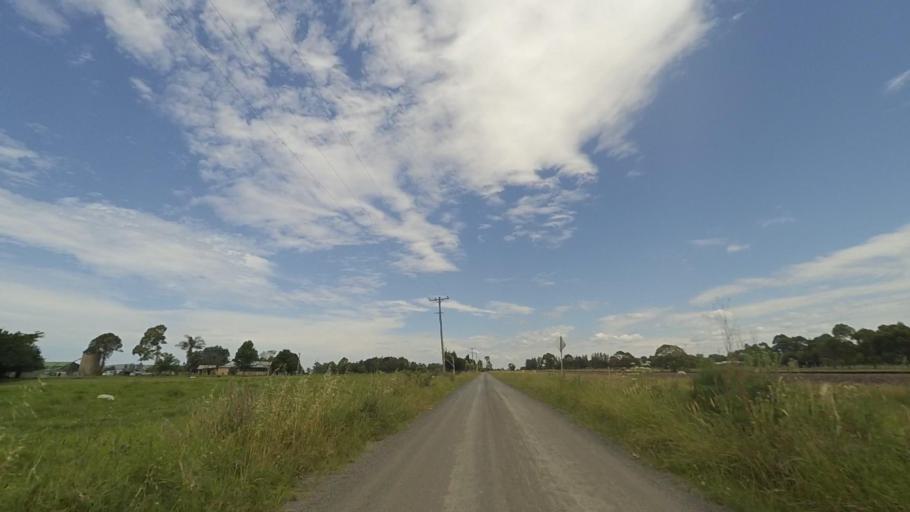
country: AU
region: New South Wales
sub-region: Shoalhaven Shire
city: Berry
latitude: -34.7913
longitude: 150.6789
